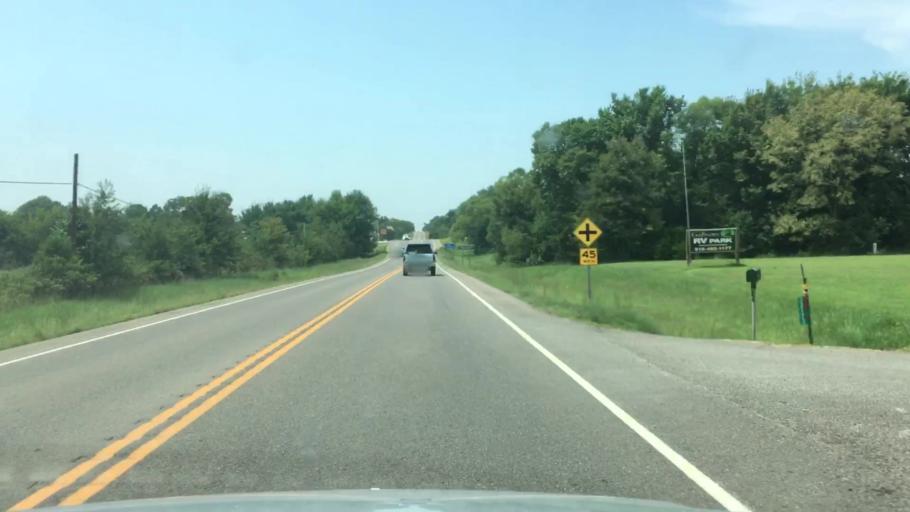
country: US
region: Oklahoma
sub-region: Wagoner County
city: Wagoner
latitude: 35.9416
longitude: -95.2935
